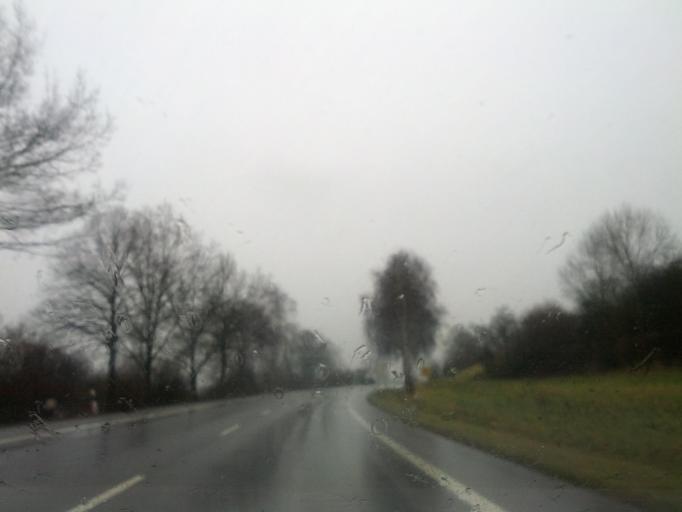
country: DE
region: Hesse
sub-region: Regierungsbezirk Kassel
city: Eschwege
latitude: 51.2101
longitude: 9.9973
